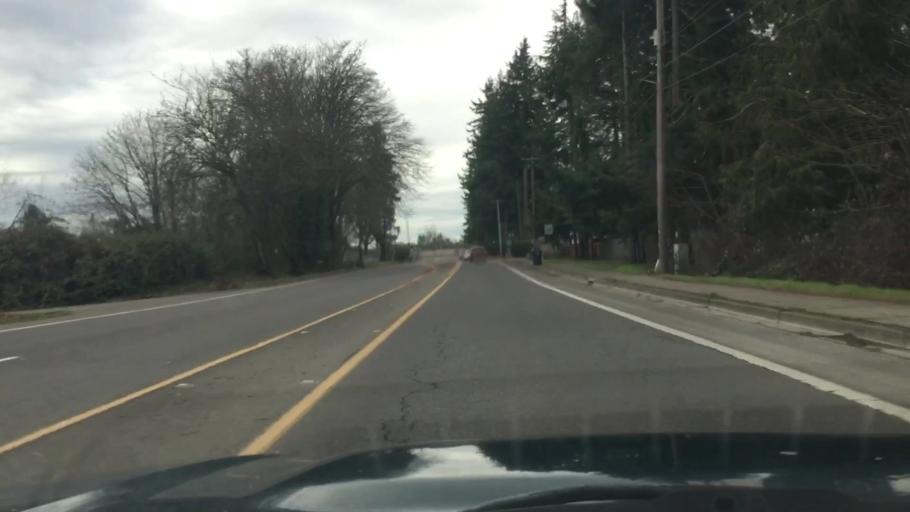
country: US
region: Oregon
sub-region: Lane County
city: Coburg
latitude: 44.1078
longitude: -123.0532
